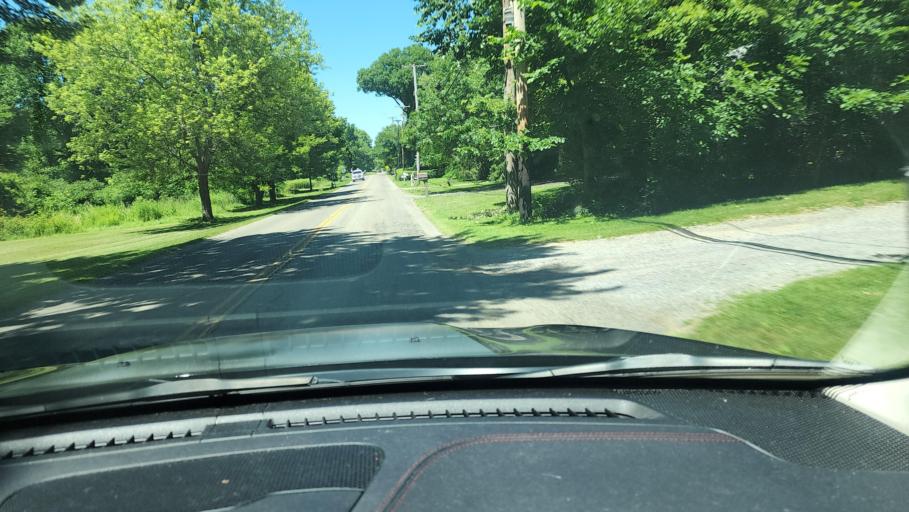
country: US
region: Ohio
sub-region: Mahoning County
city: Austintown
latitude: 41.0934
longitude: -80.7918
